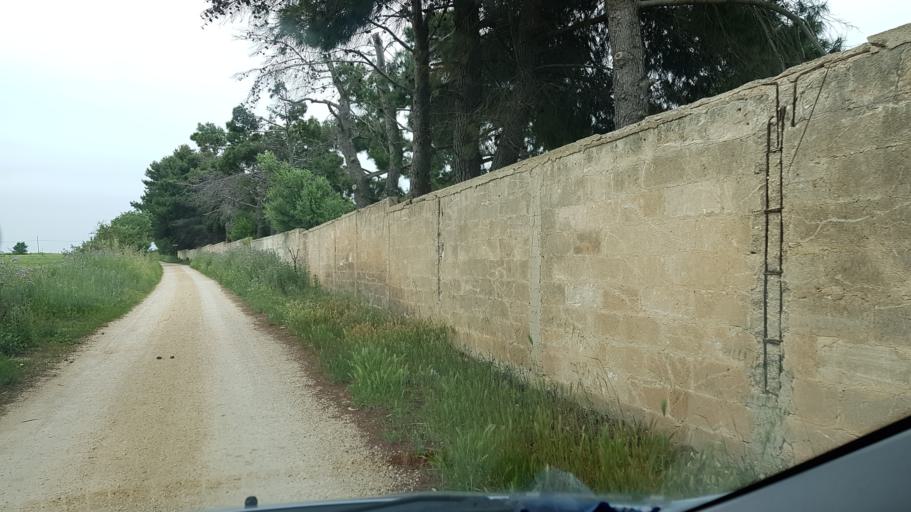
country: IT
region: Apulia
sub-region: Provincia di Brindisi
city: Brindisi
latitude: 40.6493
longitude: 17.8829
